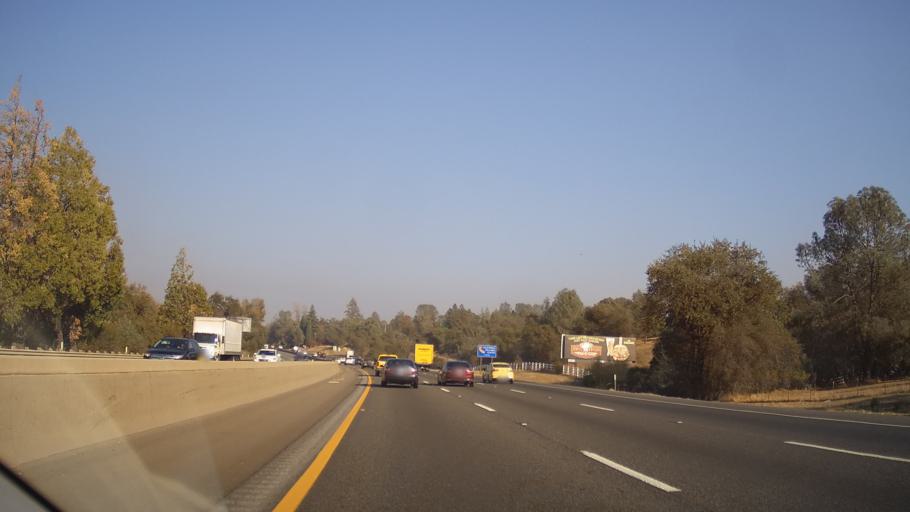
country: US
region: California
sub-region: Placer County
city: Newcastle
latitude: 38.8817
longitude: -121.1069
